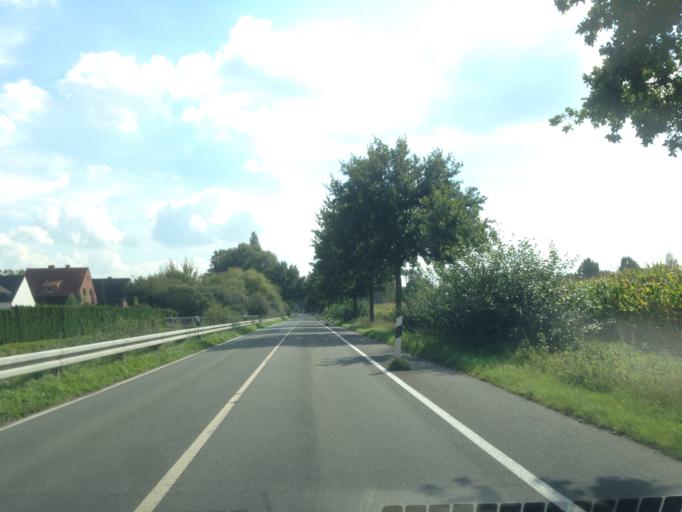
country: DE
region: North Rhine-Westphalia
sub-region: Regierungsbezirk Munster
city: Muenster
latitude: 52.0101
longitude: 7.6089
